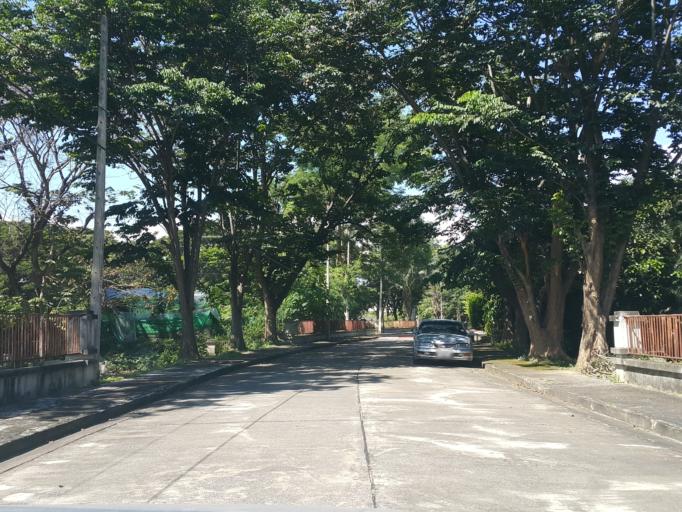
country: TH
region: Chiang Mai
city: San Sai
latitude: 18.8471
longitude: 99.0052
